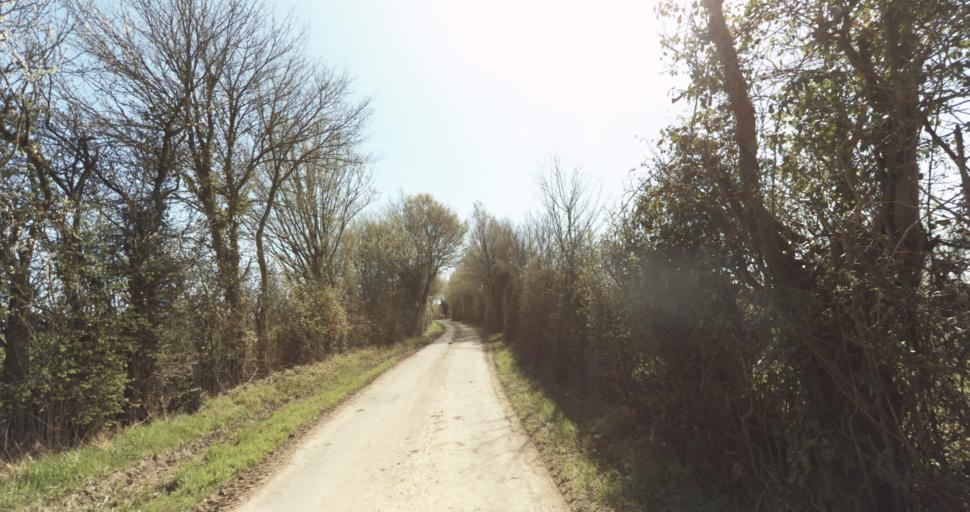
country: FR
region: Lower Normandy
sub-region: Departement du Calvados
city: Livarot
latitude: 49.0214
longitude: 0.1022
